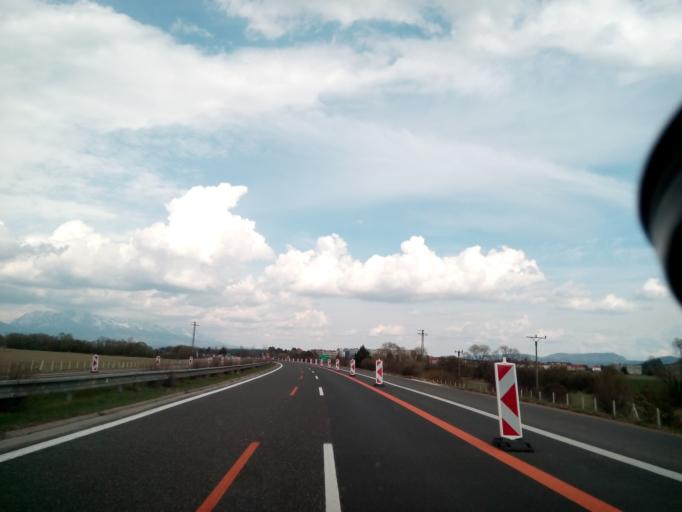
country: SK
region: Zilinsky
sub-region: Okres Zilina
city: Liptovsky Hradok
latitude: 49.0535
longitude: 19.7194
